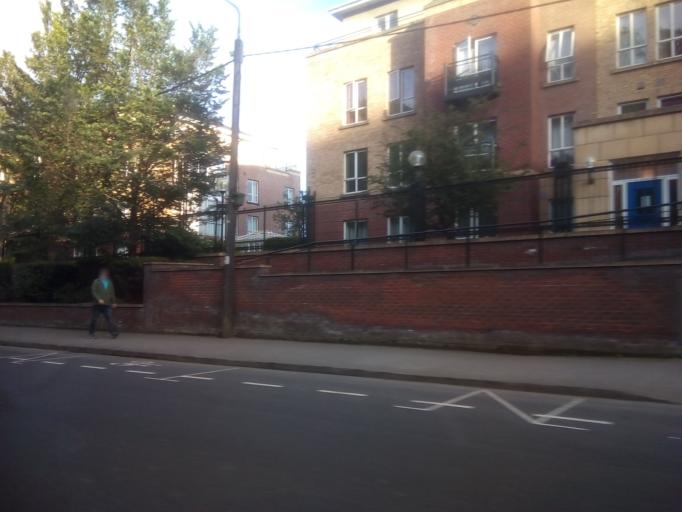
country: IE
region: Leinster
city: Rialto
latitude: 53.3458
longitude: -6.3012
